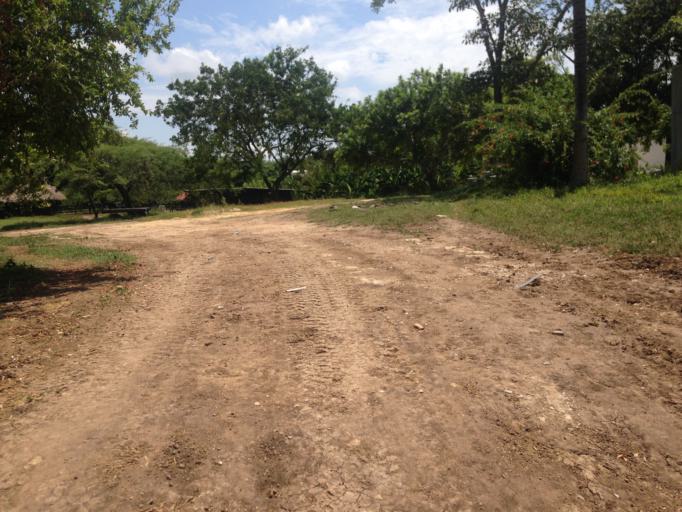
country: CO
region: Atlantico
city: Baranoa
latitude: 10.8417
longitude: -74.9037
